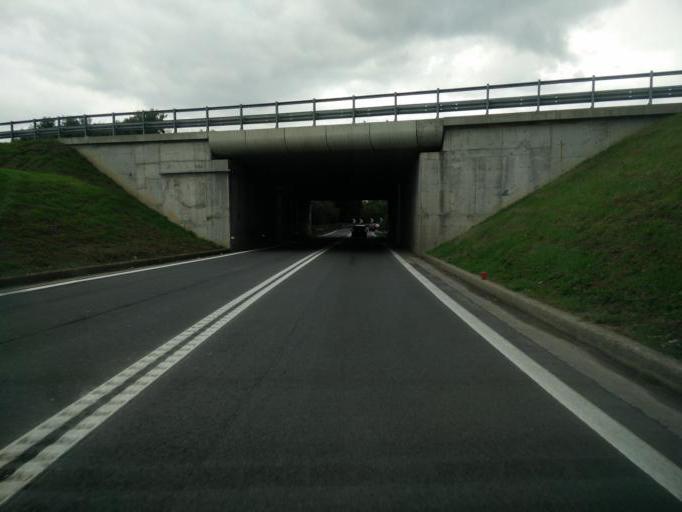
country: IT
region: Tuscany
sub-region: Province of Florence
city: Tavarnuzze
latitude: 43.7231
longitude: 11.2220
